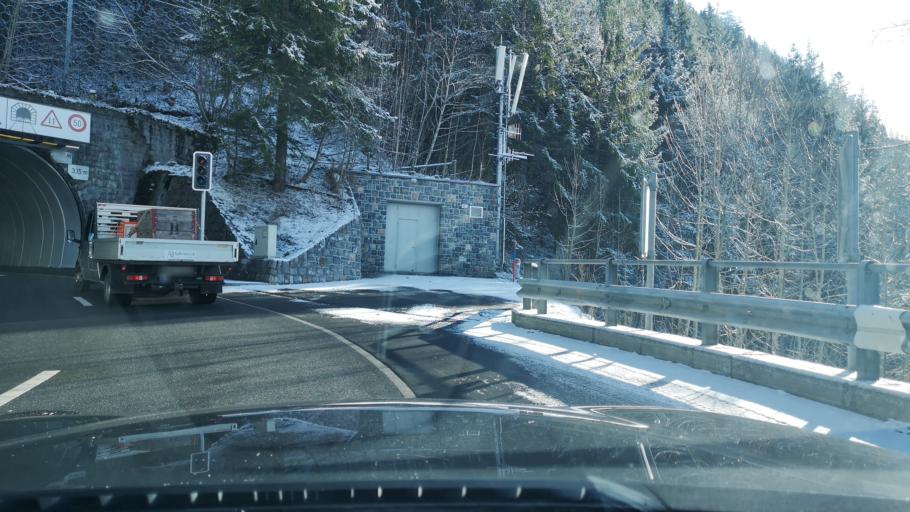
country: LI
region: Triesenberg
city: Triesenberg
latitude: 47.1161
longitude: 9.5595
